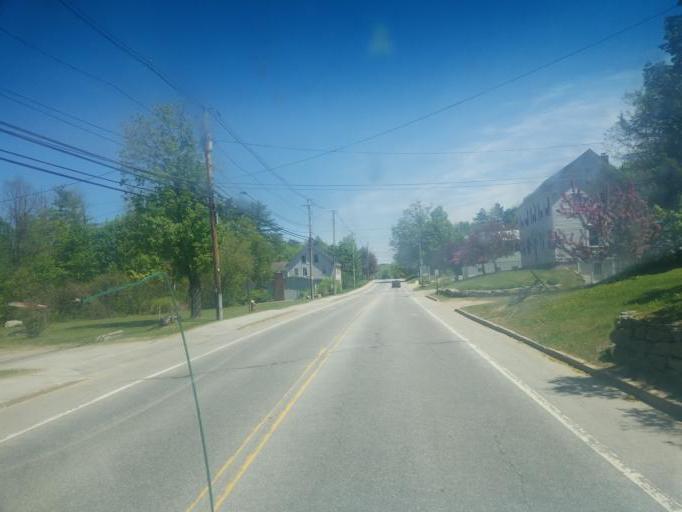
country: US
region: New Hampshire
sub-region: Grafton County
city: Plymouth
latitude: 43.7592
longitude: -71.6993
